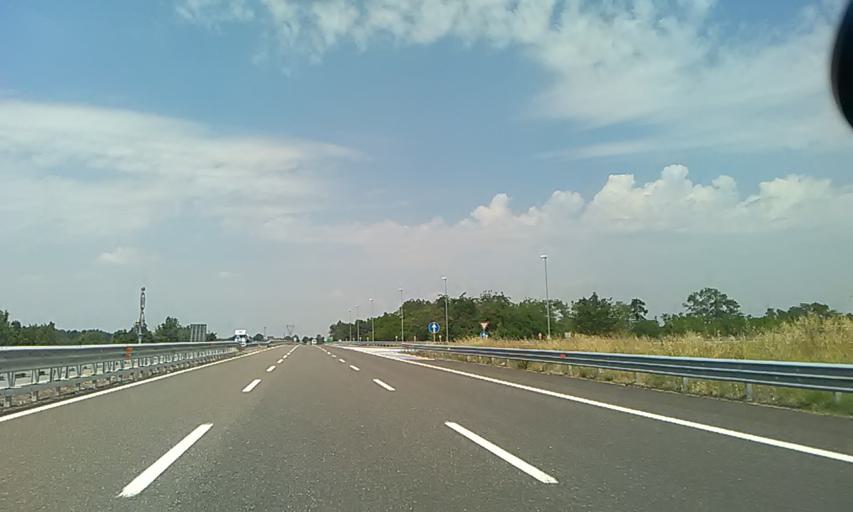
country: IT
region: Piedmont
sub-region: Provincia di Alessandria
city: Predosa
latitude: 44.7618
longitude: 8.6411
